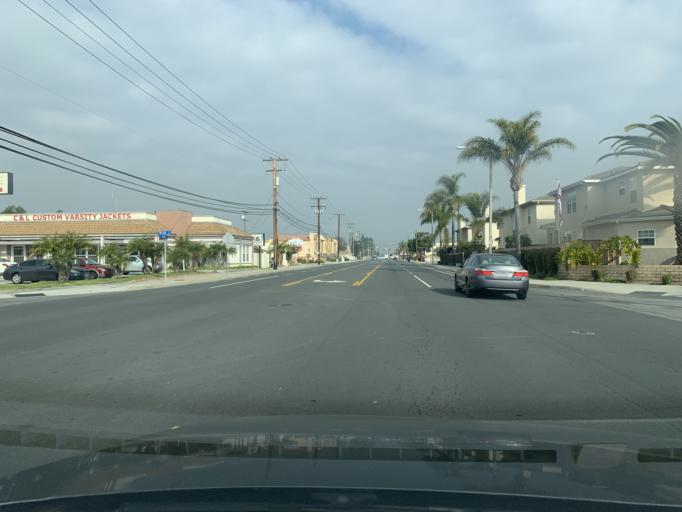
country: US
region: California
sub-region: Orange County
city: Cypress
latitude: 33.8288
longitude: -118.0369
